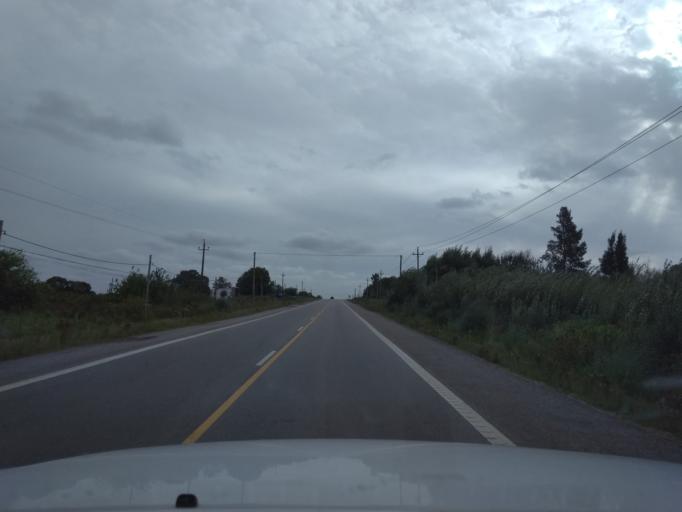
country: UY
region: Canelones
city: Joaquin Suarez
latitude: -34.6983
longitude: -56.0373
